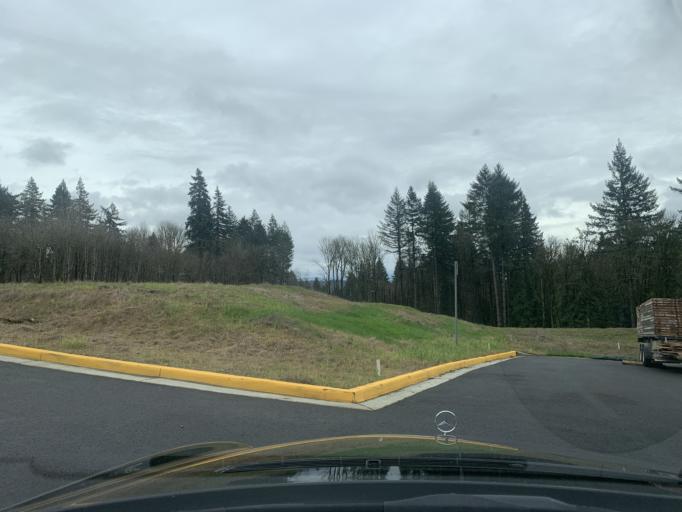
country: US
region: Oregon
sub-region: Clackamas County
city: Happy Valley
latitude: 45.4410
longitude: -122.5064
